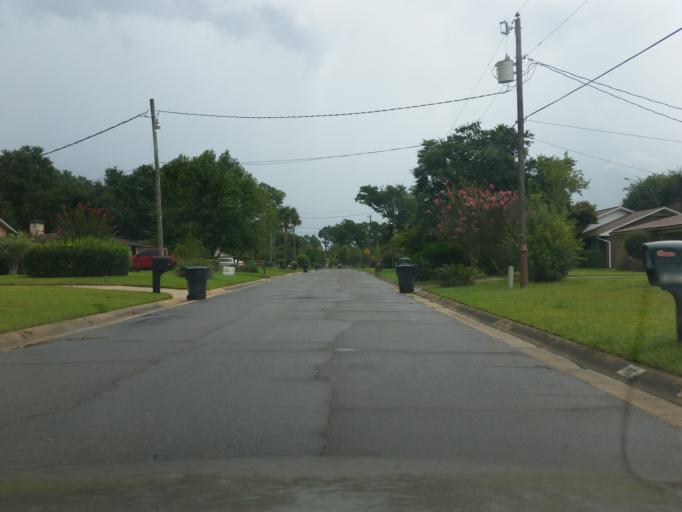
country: US
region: Florida
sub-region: Escambia County
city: Ferry Pass
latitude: 30.4901
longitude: -87.2168
